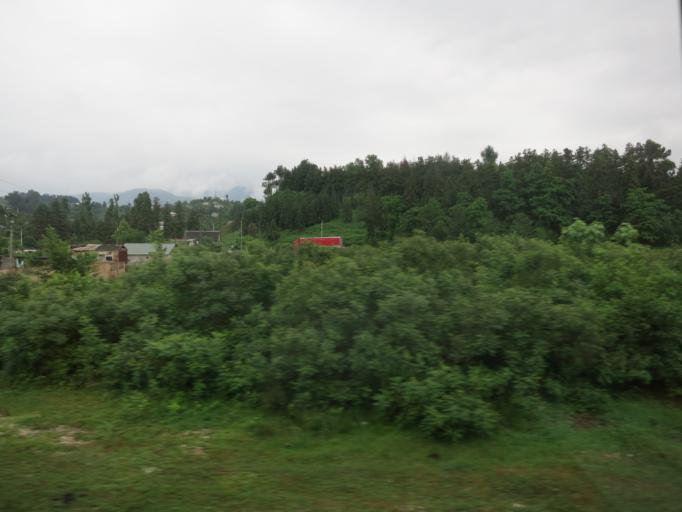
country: GE
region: Ajaria
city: Makhinjauri
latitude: 41.7431
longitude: 41.7367
